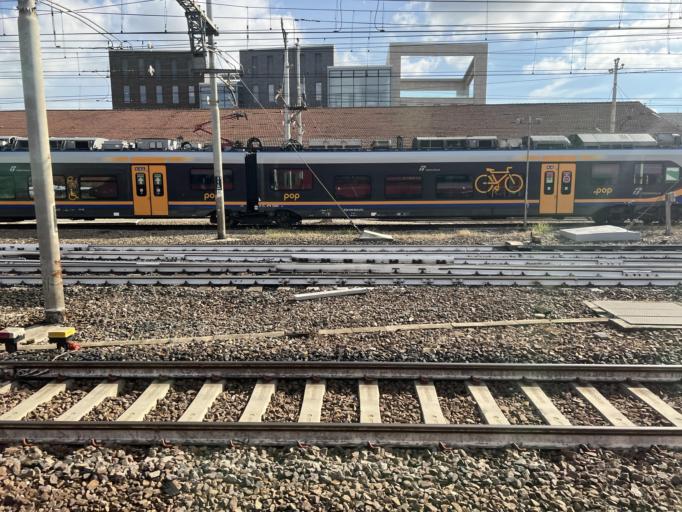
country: IT
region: Emilia-Romagna
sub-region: Provincia di Parma
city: Parma
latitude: 44.8087
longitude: 10.3350
